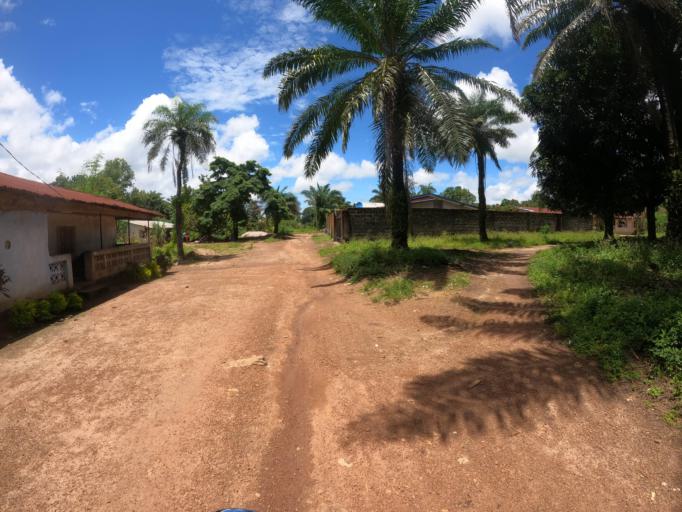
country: SL
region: Northern Province
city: Makeni
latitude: 8.8911
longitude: -12.0667
